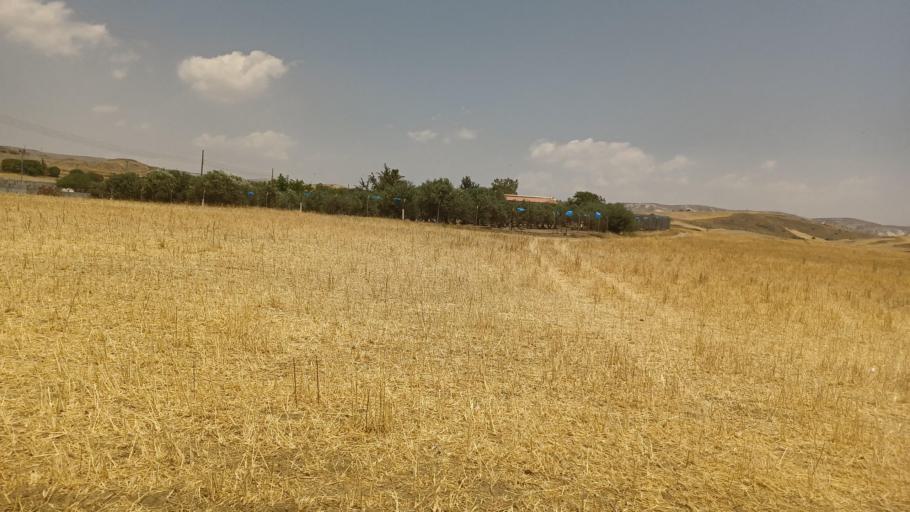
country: CY
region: Larnaka
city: Troulloi
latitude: 35.0130
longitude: 33.6077
